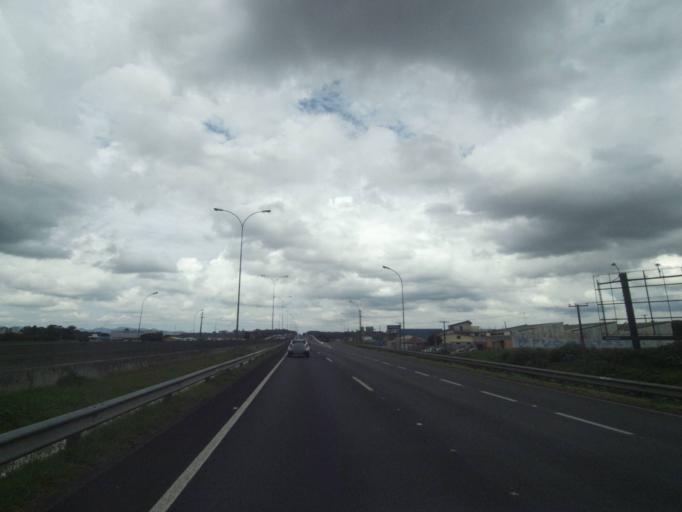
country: BR
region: Parana
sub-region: Pinhais
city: Pinhais
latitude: -25.4936
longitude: -49.1660
